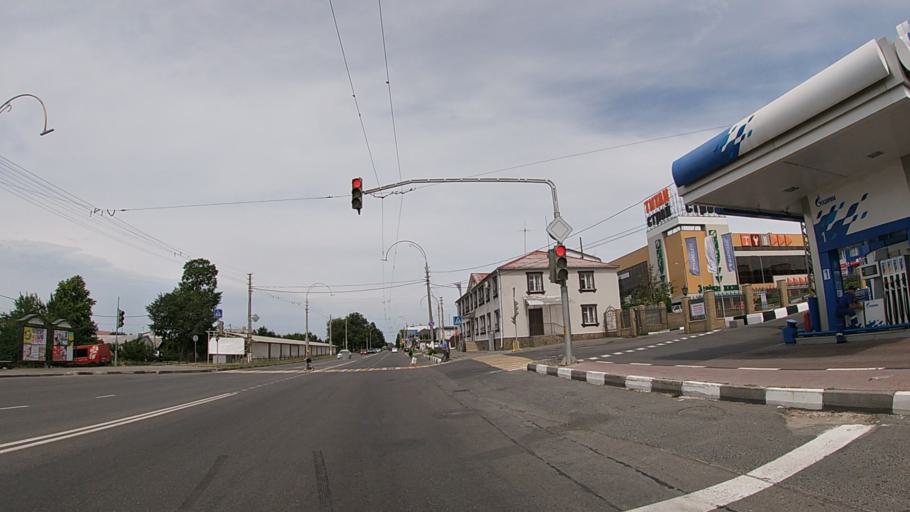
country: RU
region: Belgorod
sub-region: Belgorodskiy Rayon
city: Belgorod
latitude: 50.6026
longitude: 36.5613
